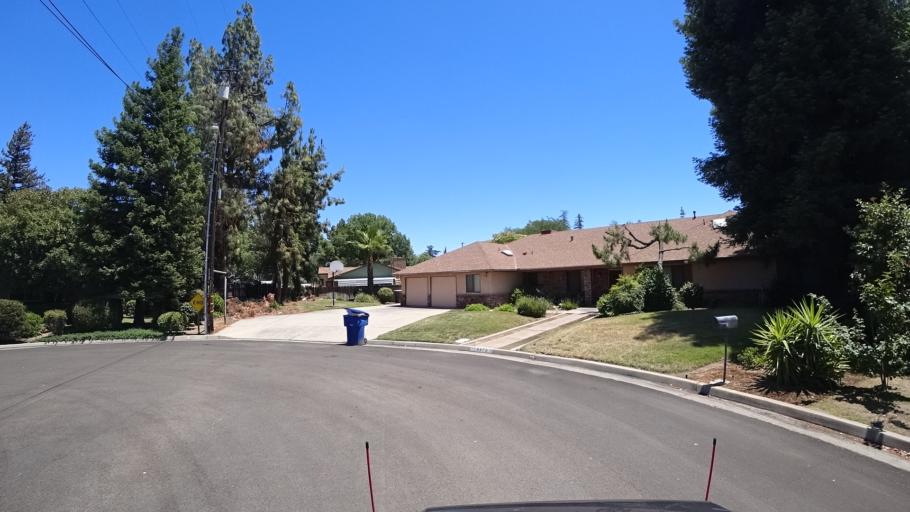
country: US
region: California
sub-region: Fresno County
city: Tarpey Village
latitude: 36.8040
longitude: -119.7507
